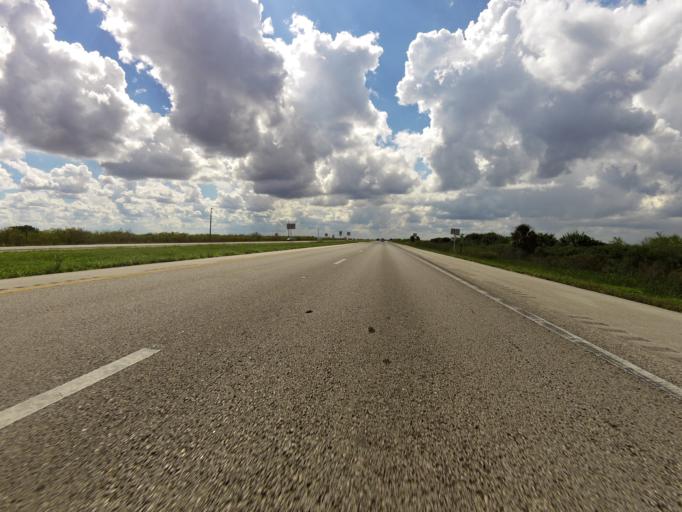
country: US
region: Florida
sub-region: Broward County
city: Weston
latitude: 26.1528
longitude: -80.7397
